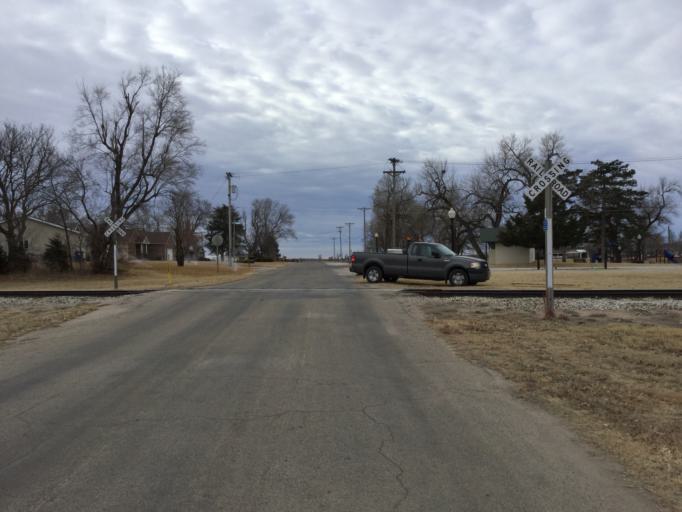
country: US
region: Kansas
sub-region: Rice County
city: Sterling
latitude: 38.2052
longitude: -98.2006
